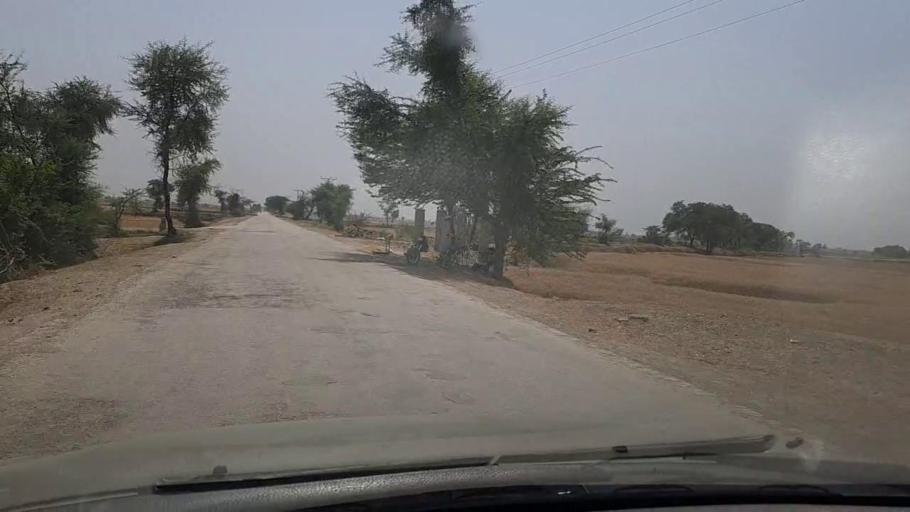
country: PK
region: Sindh
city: Miro Khan
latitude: 27.7102
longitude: 68.0647
